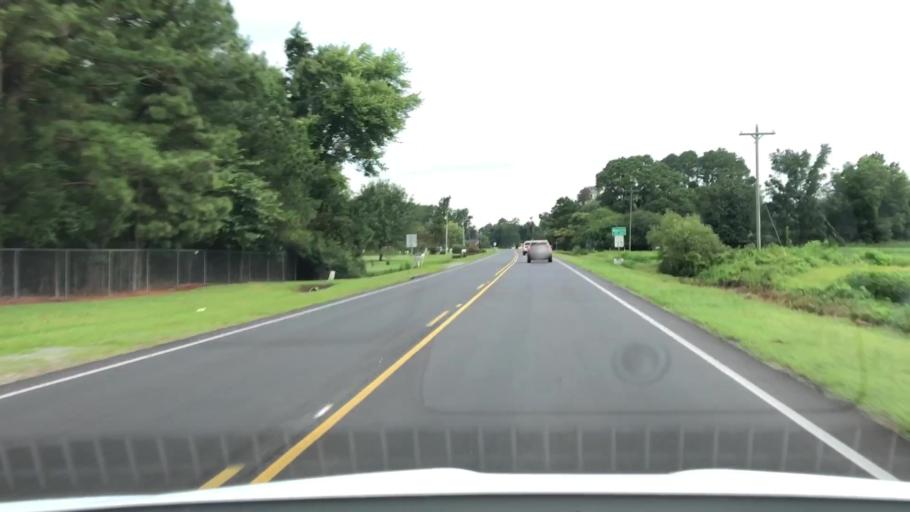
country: US
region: North Carolina
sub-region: Jones County
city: Maysville
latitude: 34.8972
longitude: -77.2206
